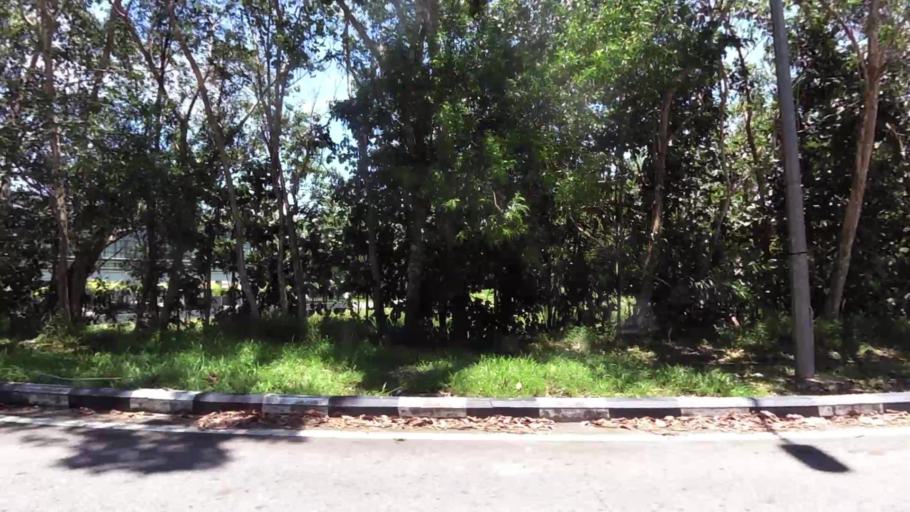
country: BN
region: Brunei and Muara
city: Bandar Seri Begawan
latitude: 4.9212
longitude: 114.9584
